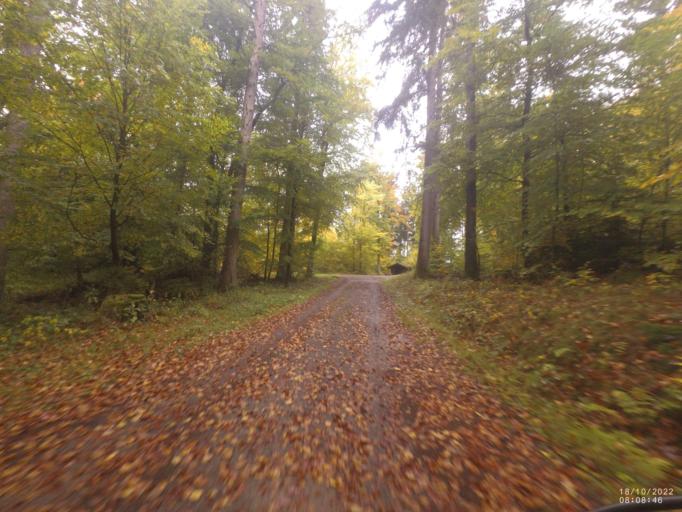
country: DE
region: Rheinland-Pfalz
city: Daun
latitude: 50.2145
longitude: 6.8267
